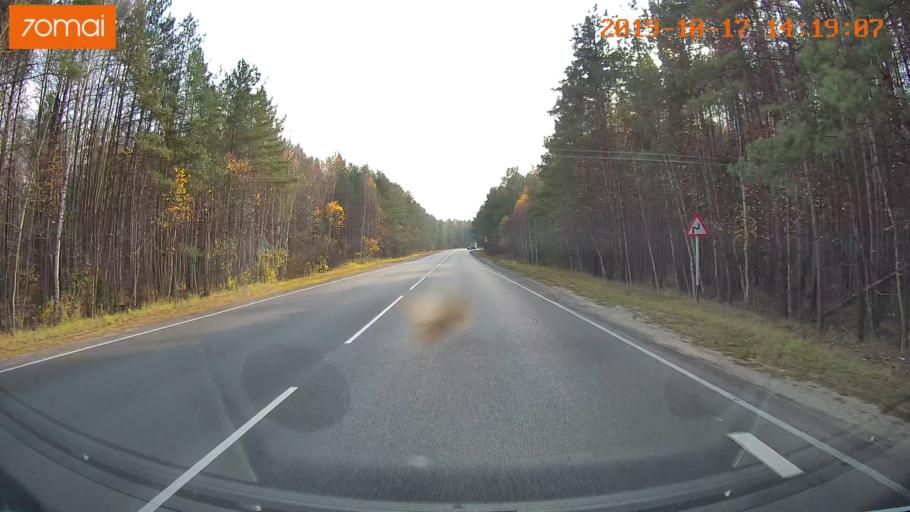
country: RU
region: Rjazan
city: Spas-Klepiki
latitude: 55.0542
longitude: 40.0241
